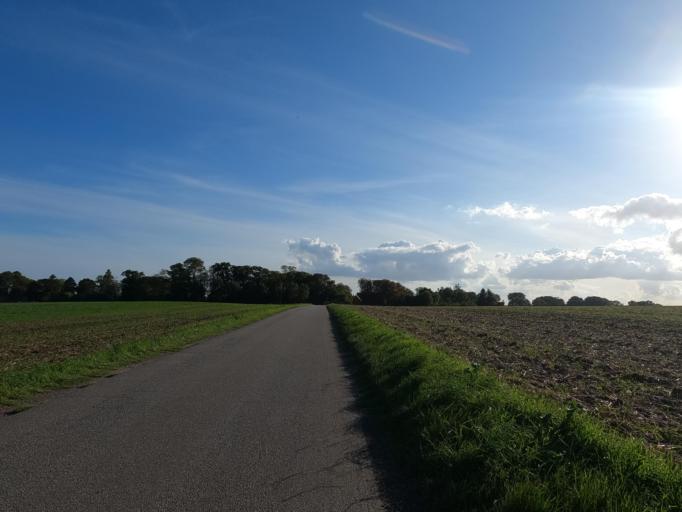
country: DE
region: Schleswig-Holstein
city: Neukirchen
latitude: 54.3373
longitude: 11.0502
